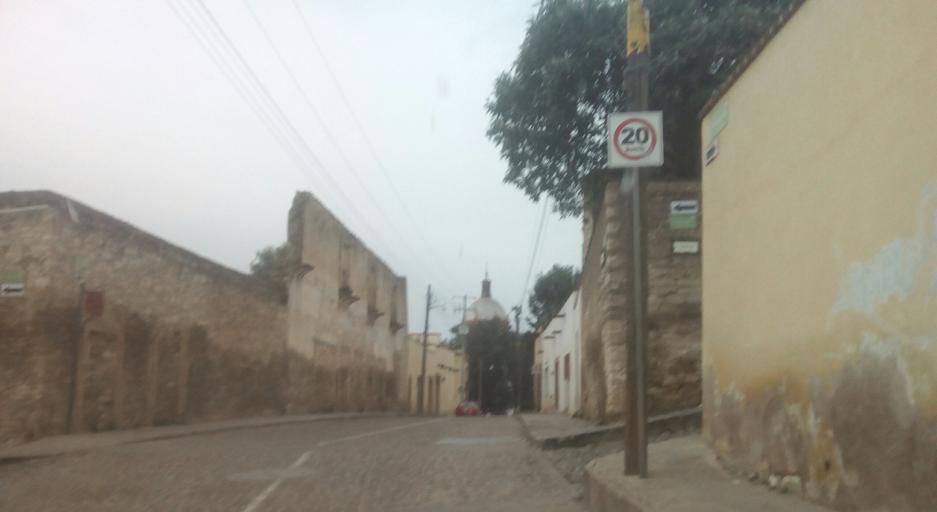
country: MX
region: Guanajuato
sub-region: San Luis de la Paz
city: San Ignacio
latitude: 21.2243
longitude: -100.4935
